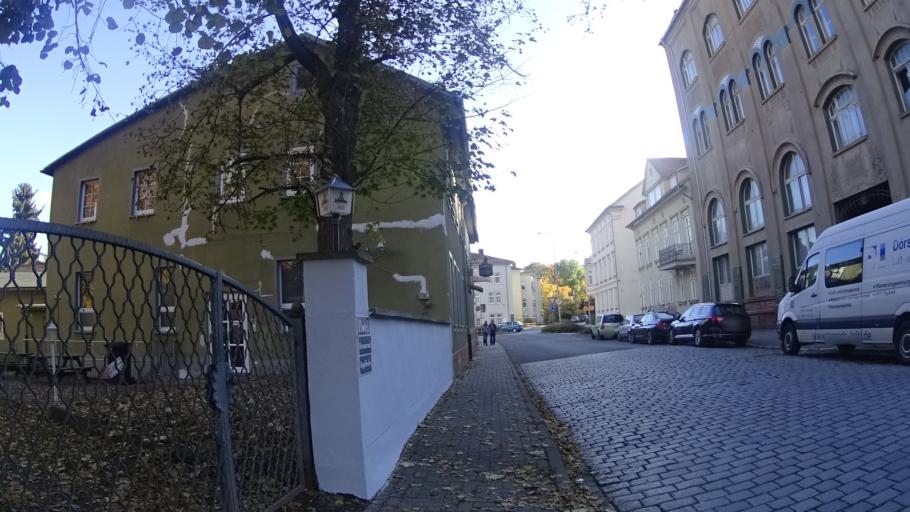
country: DE
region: Thuringia
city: Arnstadt
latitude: 50.8296
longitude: 10.9484
